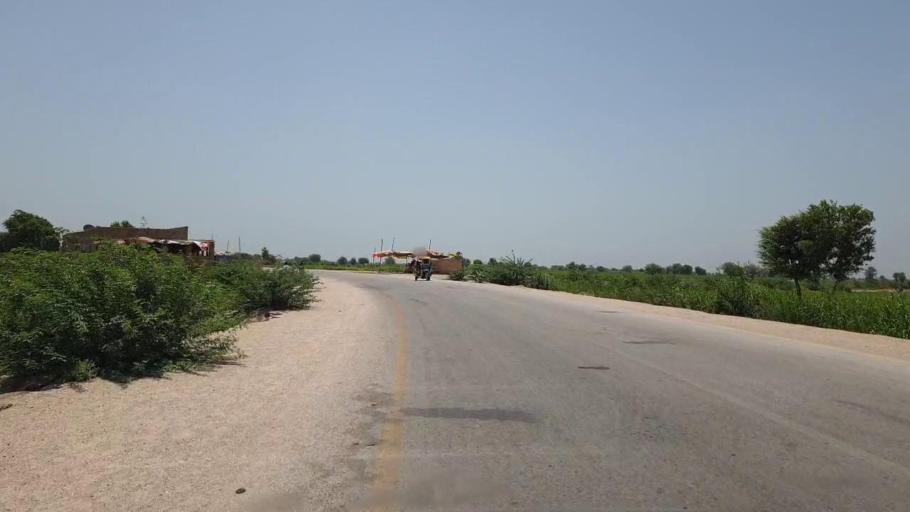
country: PK
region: Sindh
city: Sakrand
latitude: 26.1420
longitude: 68.3637
